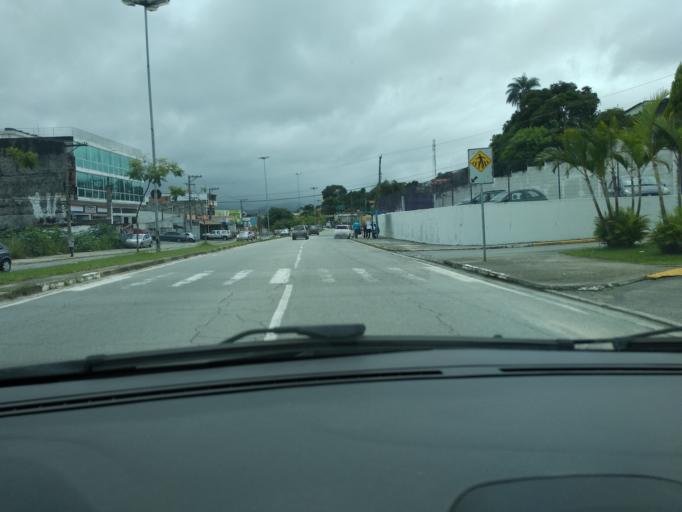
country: BR
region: Sao Paulo
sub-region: Mogi das Cruzes
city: Mogi das Cruzes
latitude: -23.5436
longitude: -46.1848
